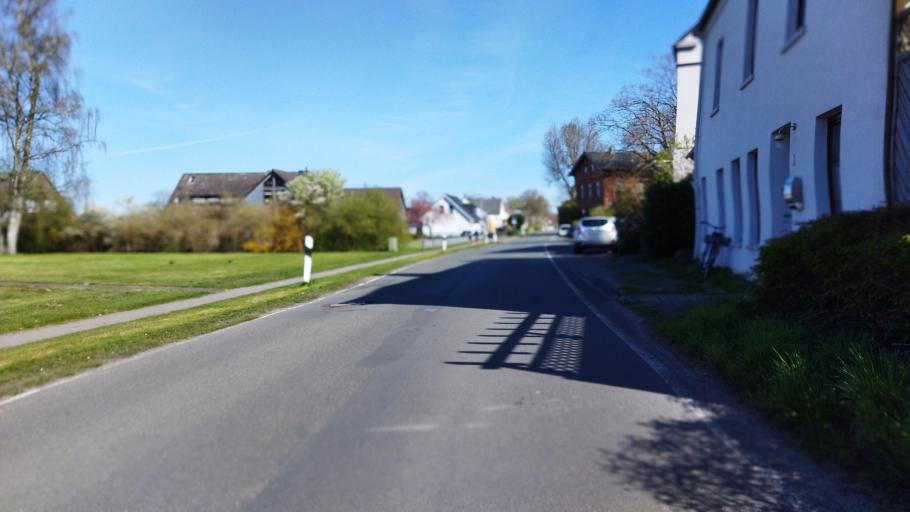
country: DE
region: Lower Saxony
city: Elsfleth
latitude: 53.2466
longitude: 8.4669
